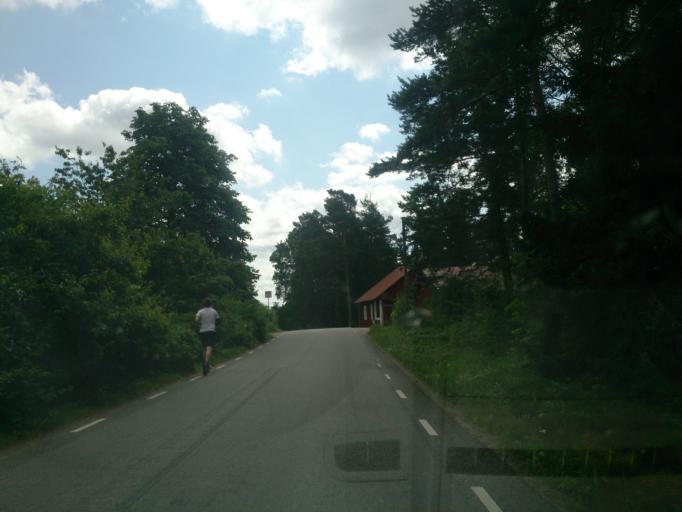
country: SE
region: OEstergoetland
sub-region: Norrkopings Kommun
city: Krokek
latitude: 58.4946
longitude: 16.5519
